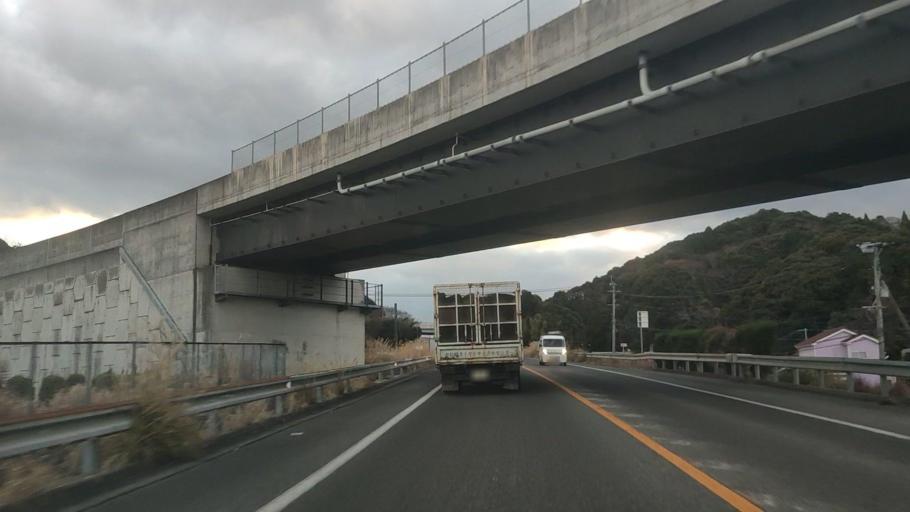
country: JP
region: Nagasaki
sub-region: Isahaya-shi
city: Isahaya
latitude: 32.8166
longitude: 129.9664
